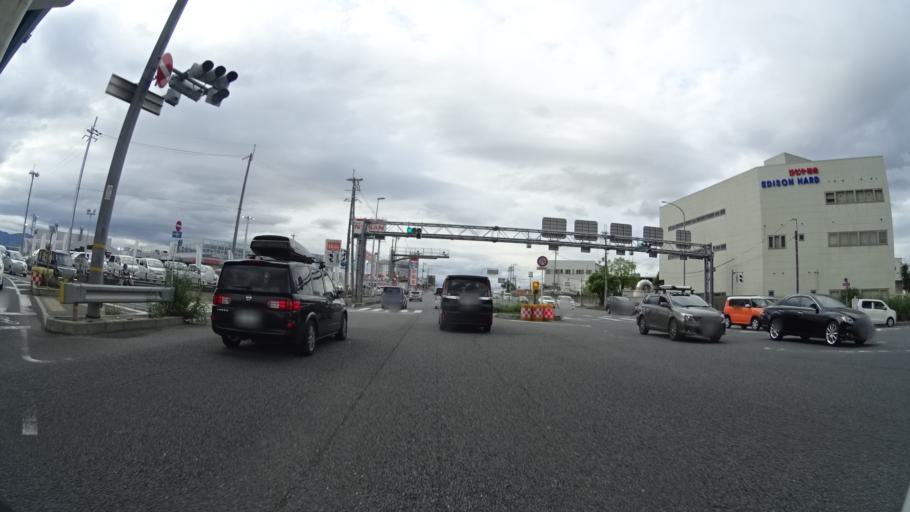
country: JP
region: Kyoto
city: Yawata
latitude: 34.8975
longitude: 135.7439
